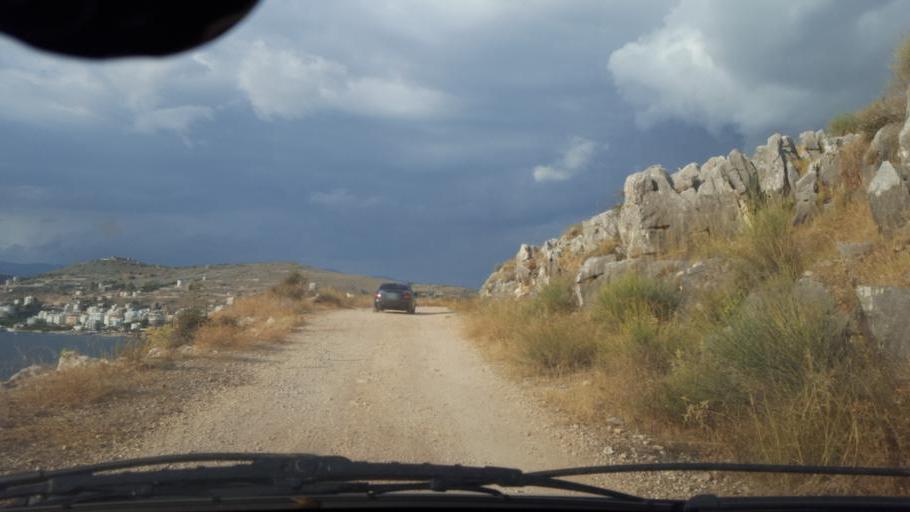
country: AL
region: Vlore
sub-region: Rrethi i Sarandes
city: Sarande
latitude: 39.8415
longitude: 20.0147
